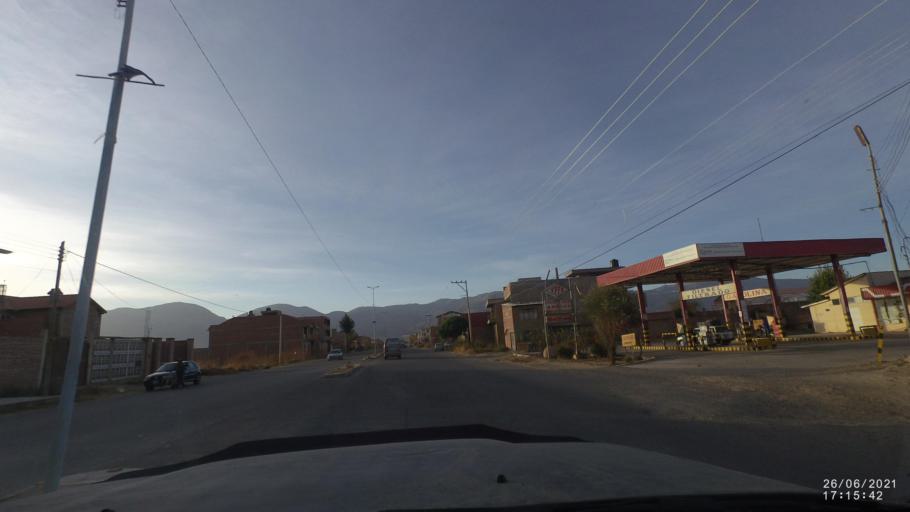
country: BO
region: Cochabamba
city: Cliza
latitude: -17.5685
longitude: -65.9354
